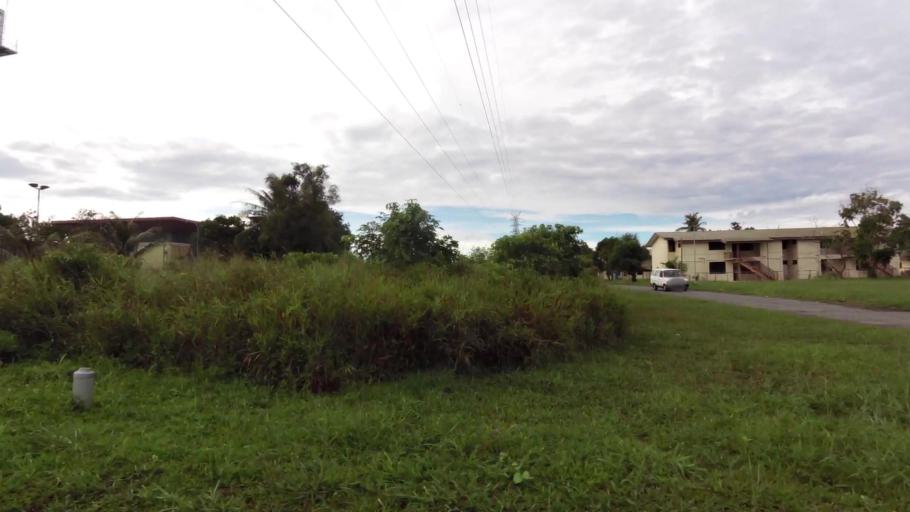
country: BN
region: Belait
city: Seria
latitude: 4.6104
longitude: 114.3409
